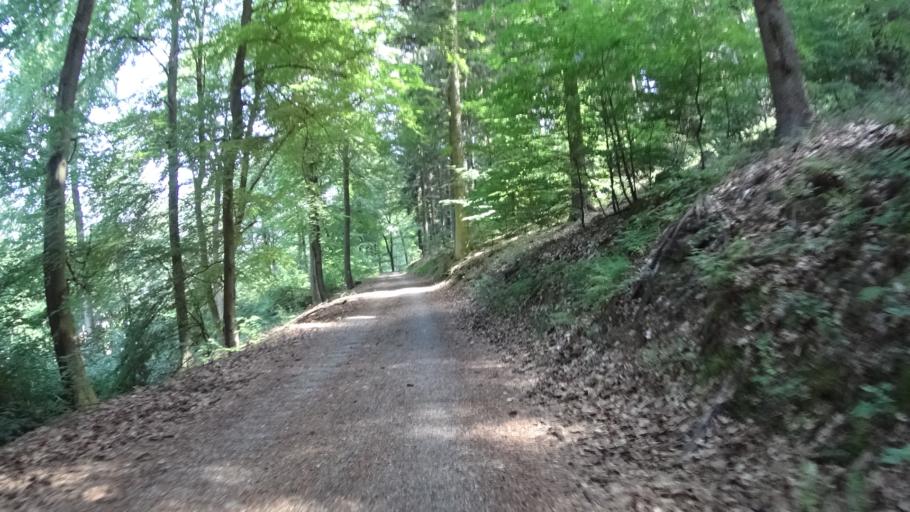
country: DE
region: Baden-Wuerttemberg
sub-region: Karlsruhe Region
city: Wilhelmsfeld
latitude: 49.4569
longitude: 8.7706
